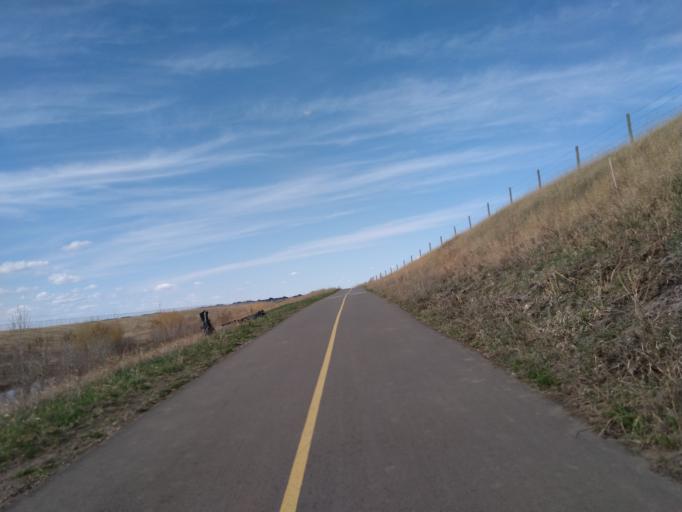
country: CA
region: Alberta
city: Chestermere
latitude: 51.0250
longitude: -113.9236
